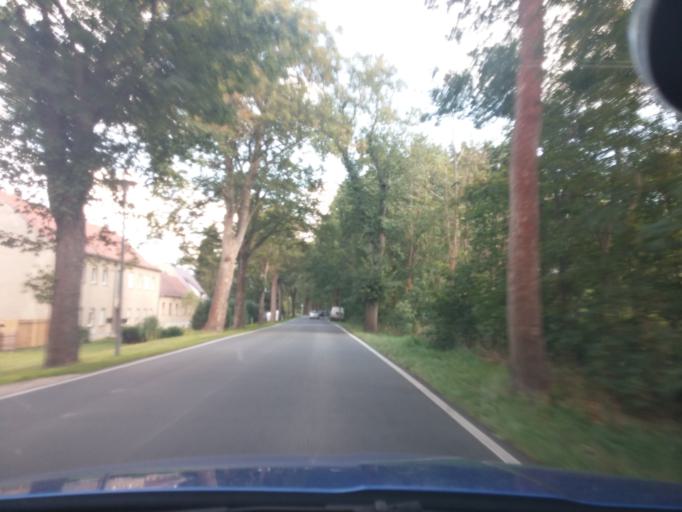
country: DE
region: Brandenburg
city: Halbe
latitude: 52.1106
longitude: 13.6831
